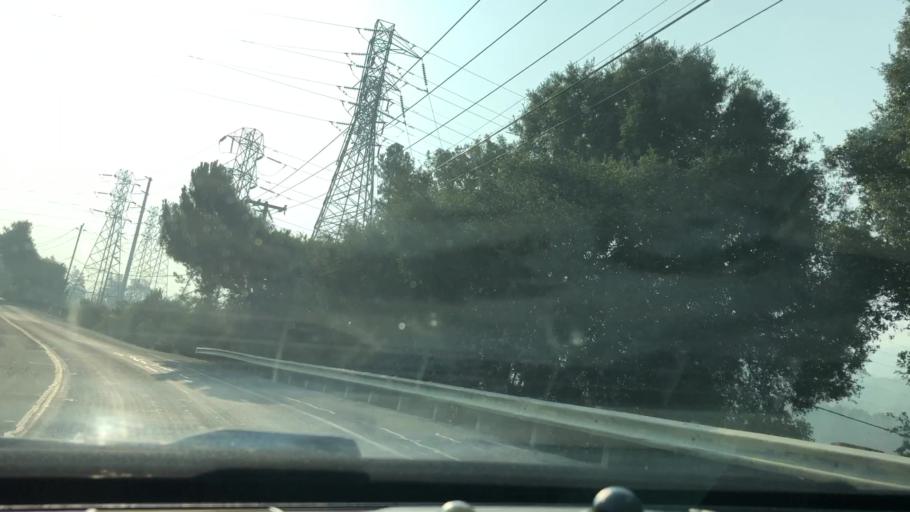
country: US
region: California
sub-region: Contra Costa County
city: Orinda
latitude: 37.9061
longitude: -122.2109
